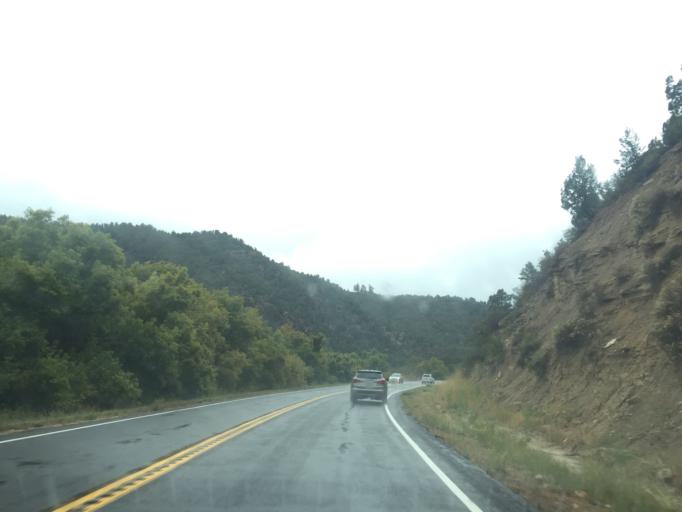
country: US
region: Utah
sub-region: Kane County
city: Kanab
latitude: 37.3548
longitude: -112.5985
